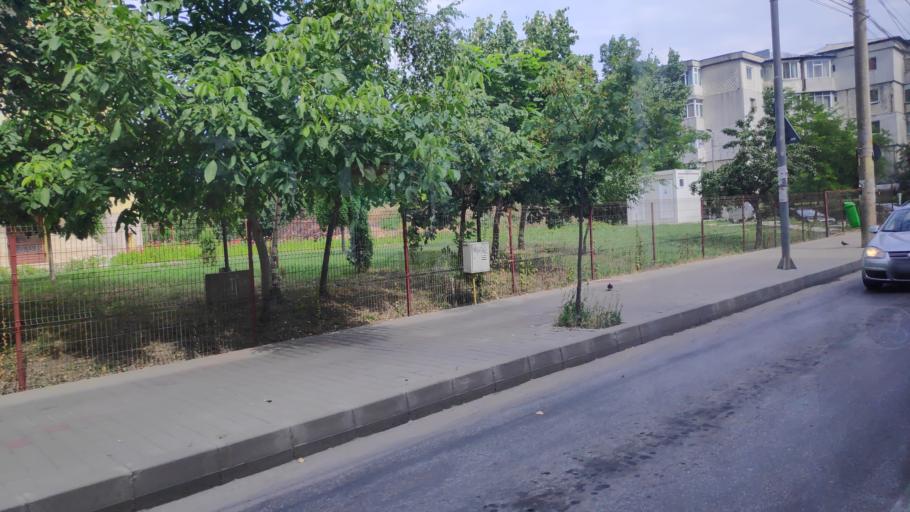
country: RO
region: Iasi
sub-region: Municipiul Iasi
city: Iasi
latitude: 47.1532
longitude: 27.5711
